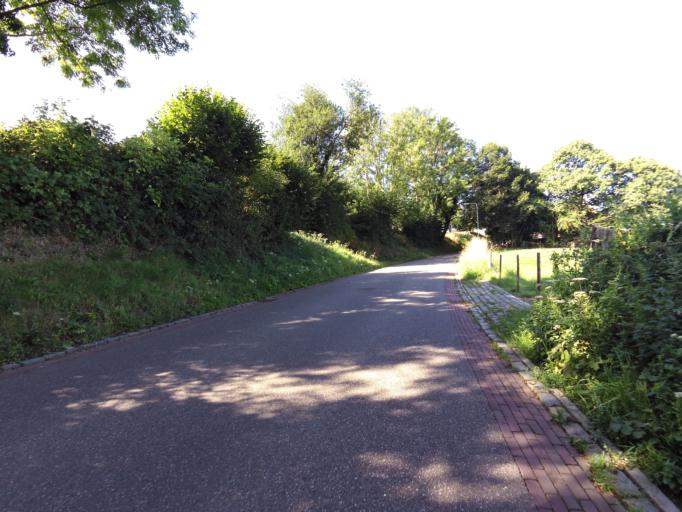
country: BE
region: Wallonia
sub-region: Province de Liege
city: Plombieres
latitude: 50.7830
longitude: 5.9022
